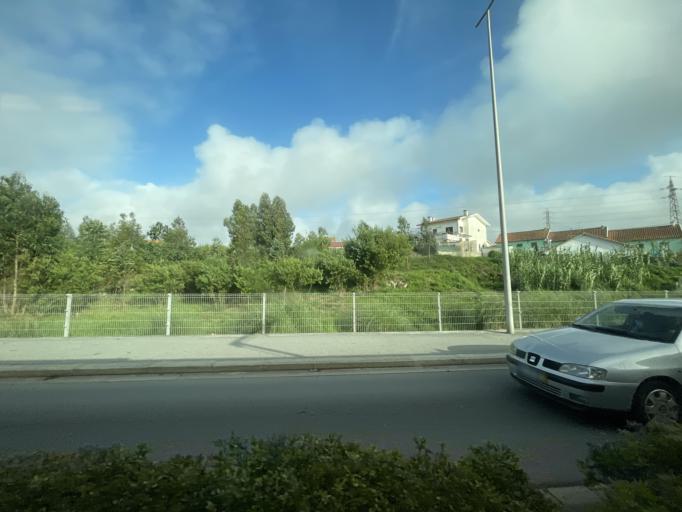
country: PT
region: Porto
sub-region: Vila do Conde
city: Vila do Conde
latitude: 41.3564
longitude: -8.7375
